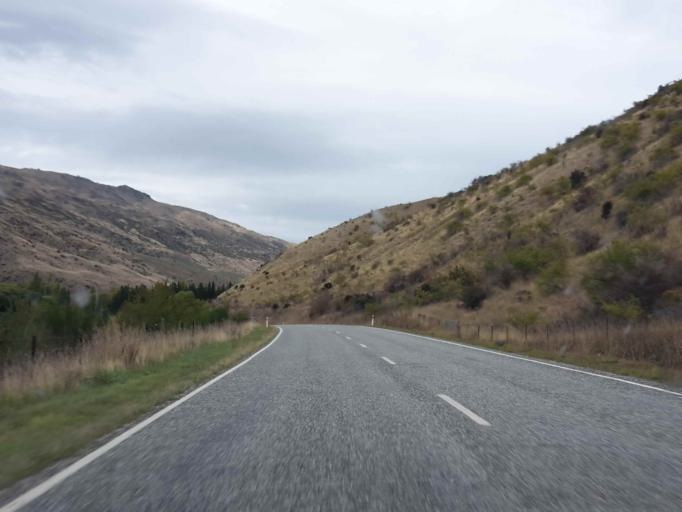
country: NZ
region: Otago
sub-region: Queenstown-Lakes District
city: Wanaka
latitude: -44.8252
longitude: 169.0608
